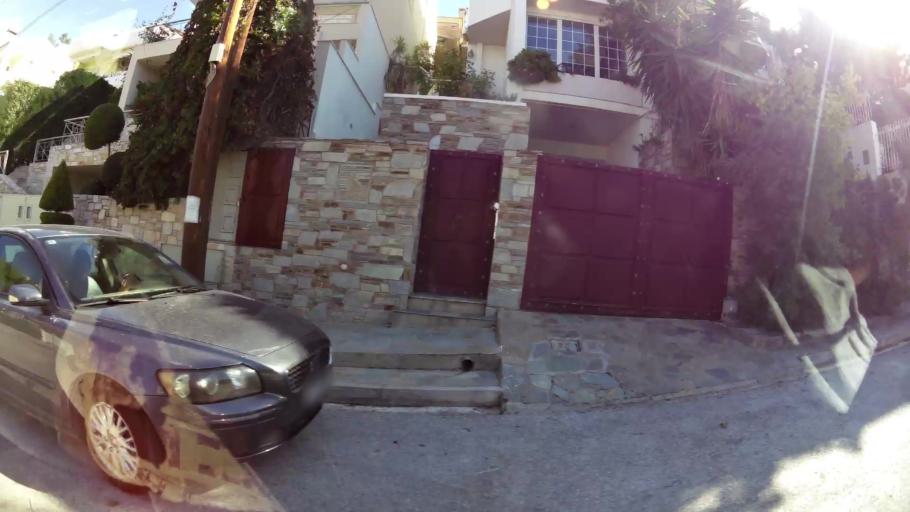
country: GR
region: Attica
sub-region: Nomarchia Anatolikis Attikis
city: Voula
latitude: 37.8573
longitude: 23.7788
